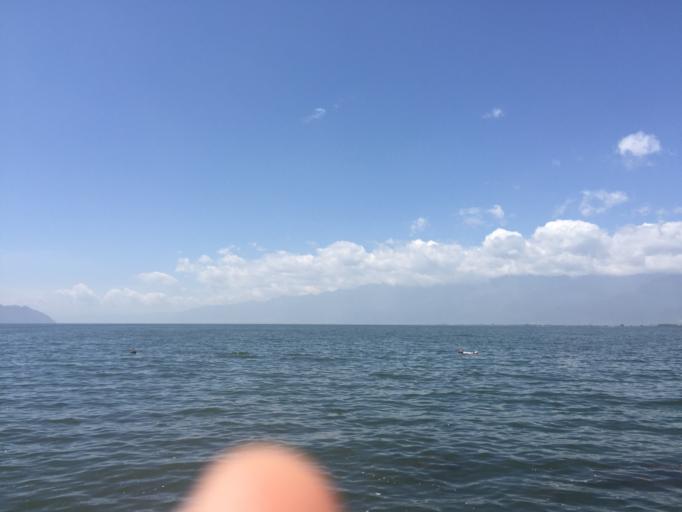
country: CN
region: Yunnan
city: Yuhu
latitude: 25.9042
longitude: 100.1898
